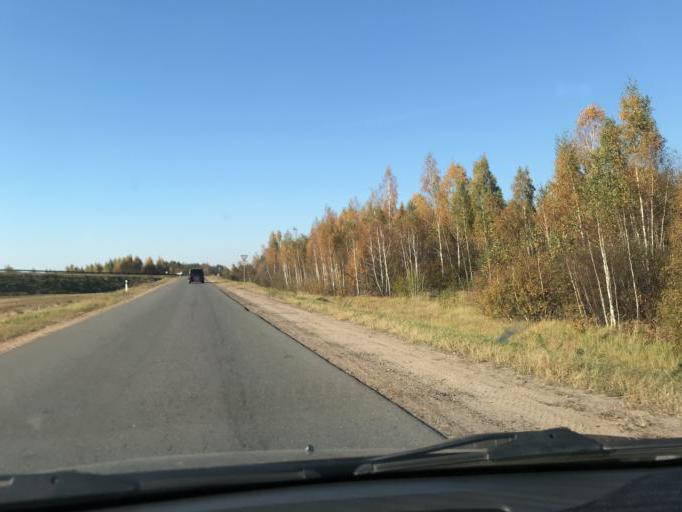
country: BY
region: Mogilev
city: Babruysk
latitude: 53.0809
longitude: 29.0688
